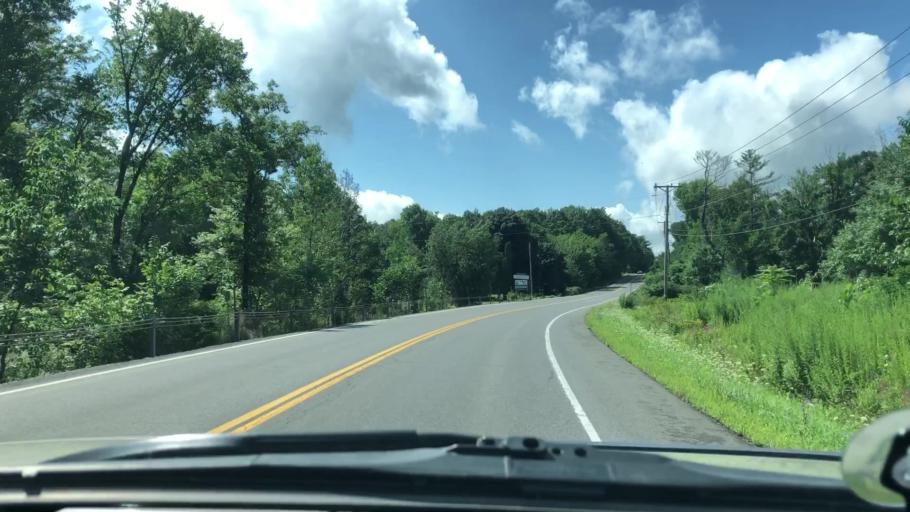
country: US
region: New York
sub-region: Greene County
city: Cairo
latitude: 42.2676
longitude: -73.9747
